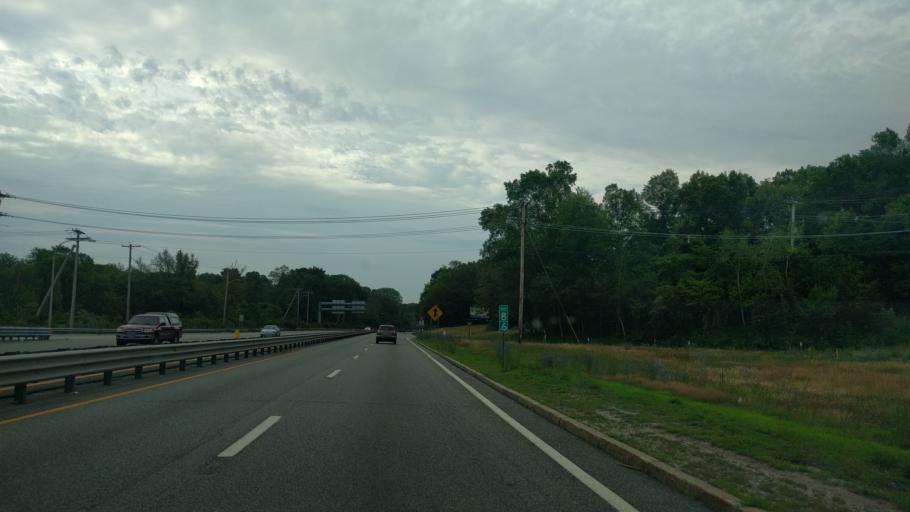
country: US
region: Rhode Island
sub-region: Providence County
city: Cumberland Hill
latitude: 41.9340
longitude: -71.4657
